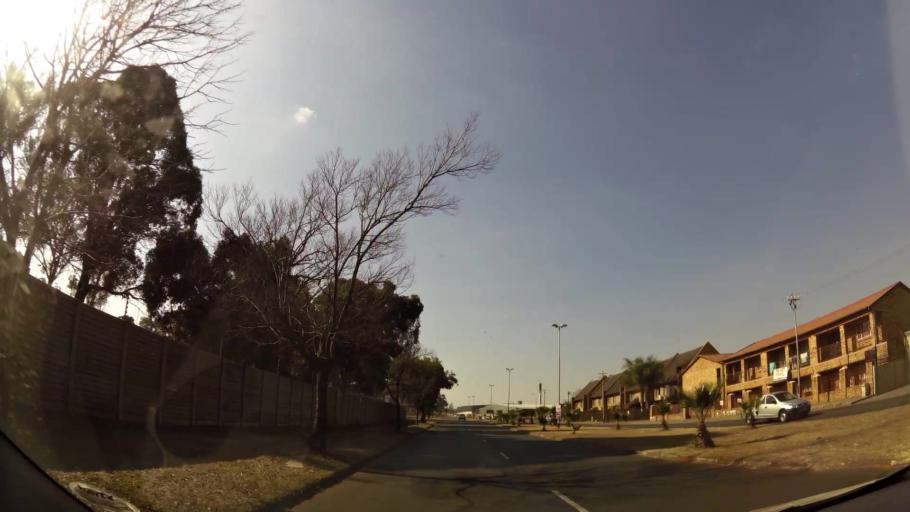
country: ZA
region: Gauteng
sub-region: West Rand District Municipality
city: Randfontein
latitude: -26.1653
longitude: 27.7072
